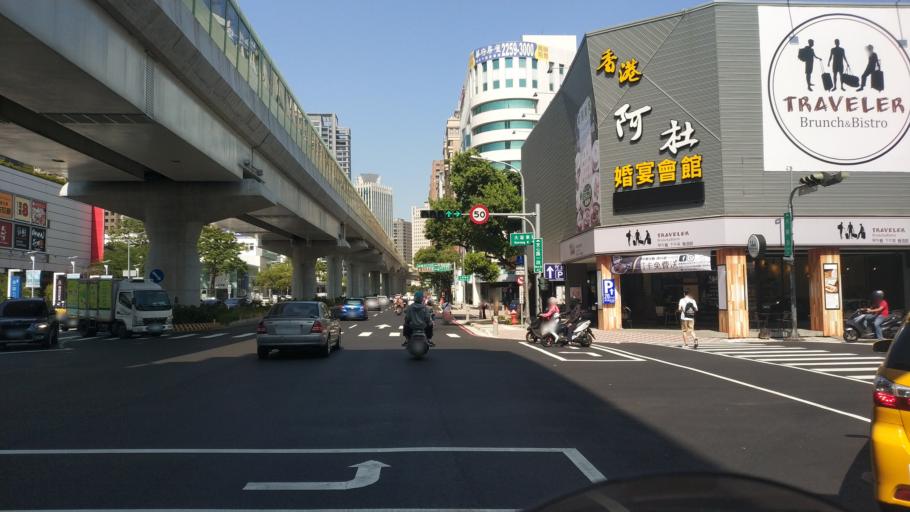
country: TW
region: Taiwan
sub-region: Taichung City
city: Taichung
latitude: 24.1535
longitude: 120.6469
